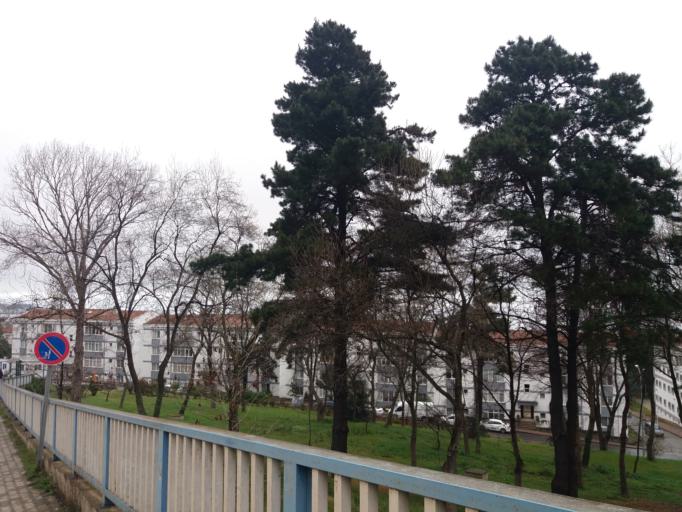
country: TR
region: Trabzon
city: Trabzon
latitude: 40.9943
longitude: 39.7677
